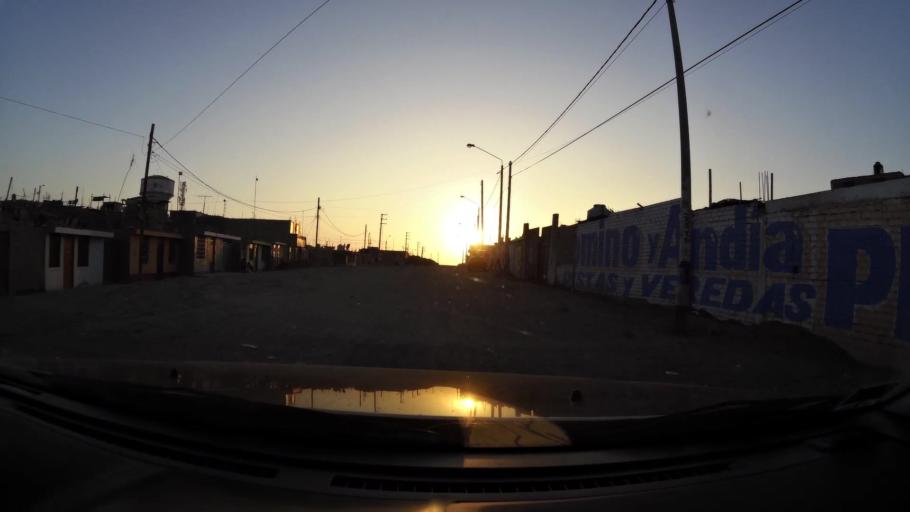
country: PE
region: Ica
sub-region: Provincia de Pisco
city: San Clemente
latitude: -13.6754
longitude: -76.1558
